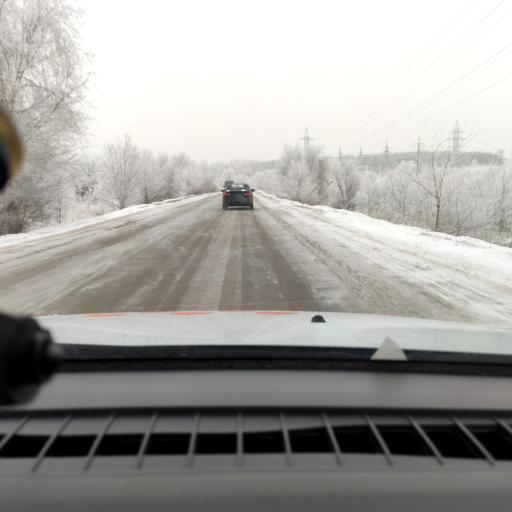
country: RU
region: Samara
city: Samara
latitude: 53.1124
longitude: 50.2247
